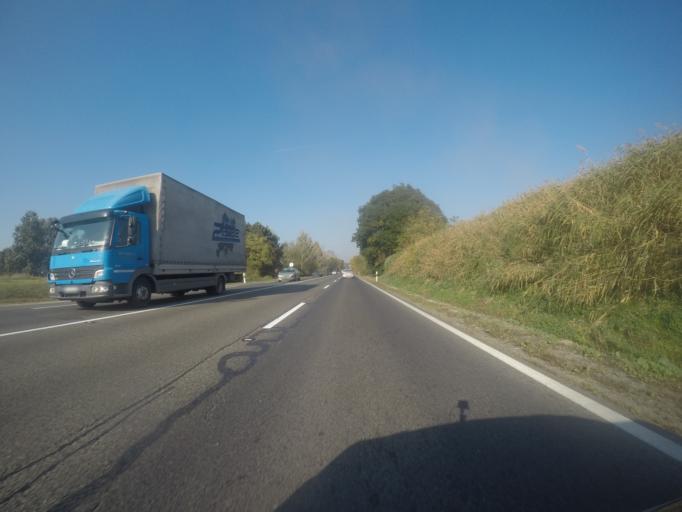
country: HU
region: Fejer
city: Baracs
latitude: 46.9165
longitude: 18.9283
